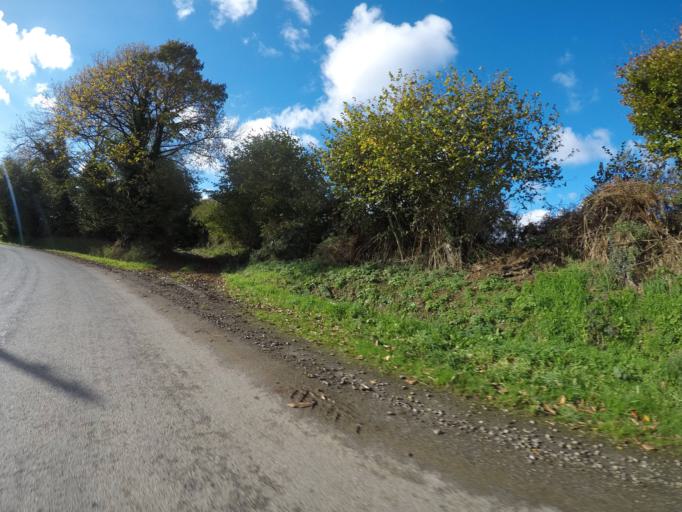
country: FR
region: Brittany
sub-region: Departement des Cotes-d'Armor
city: Bourbriac
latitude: 48.4652
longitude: -3.2425
